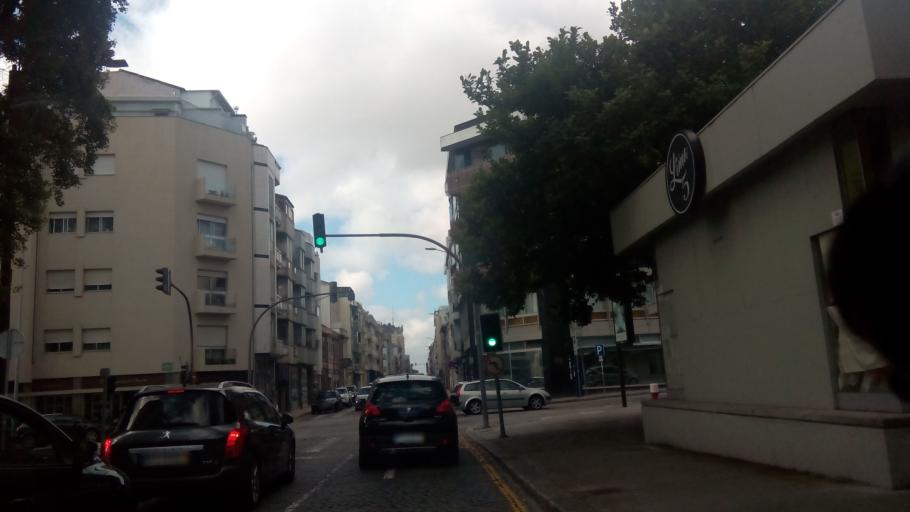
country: PT
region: Porto
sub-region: Porto
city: Porto
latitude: 41.1617
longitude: -8.6002
